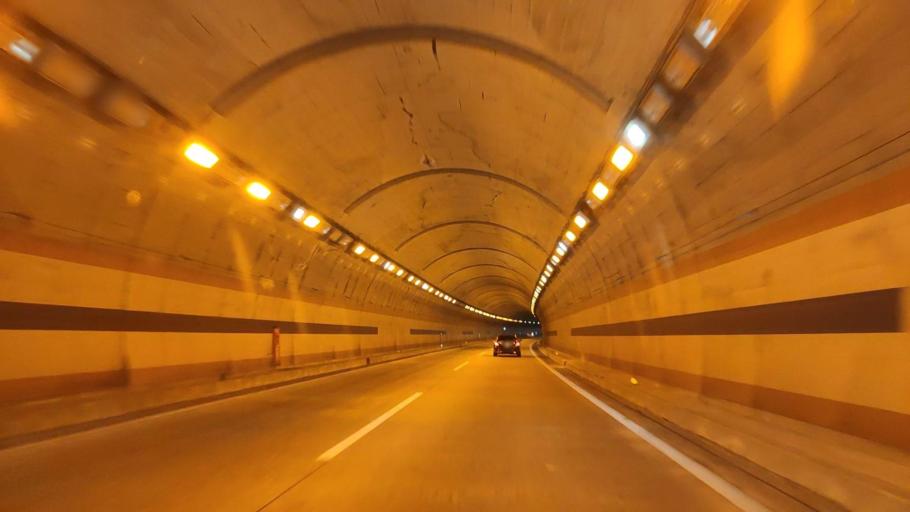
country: JP
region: Okayama
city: Kurashiki
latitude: 34.6167
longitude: 133.7398
